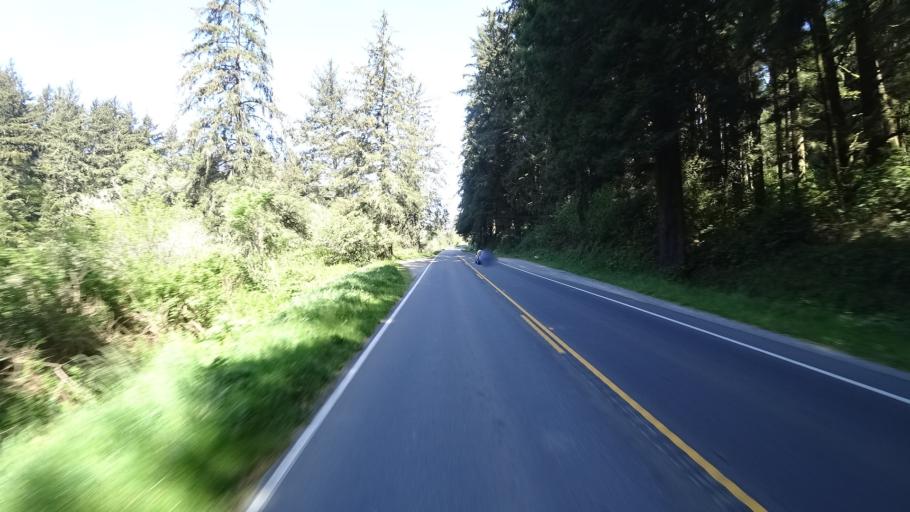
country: US
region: California
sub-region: Del Norte County
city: Bertsch-Oceanview
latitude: 41.5881
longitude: -124.0940
